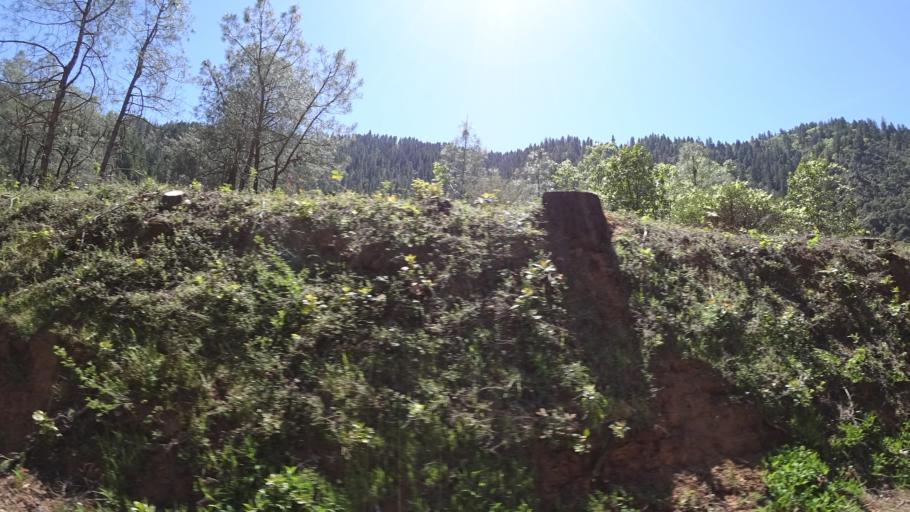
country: US
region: California
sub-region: Humboldt County
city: Willow Creek
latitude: 40.7838
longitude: -123.4226
